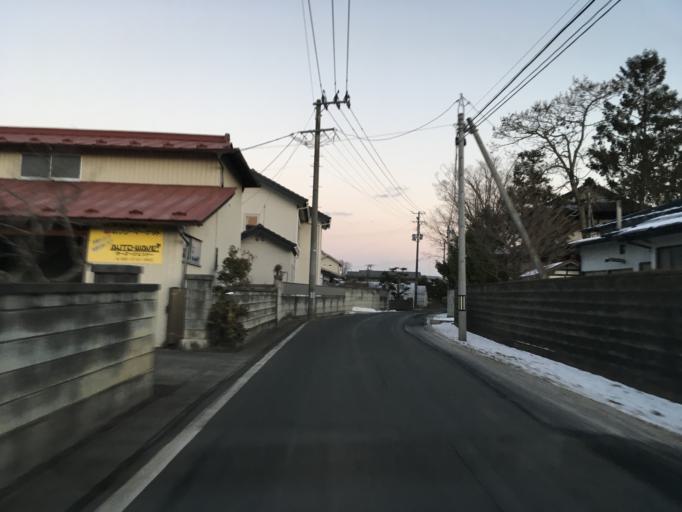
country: JP
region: Iwate
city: Ichinoseki
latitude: 38.7794
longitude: 141.1477
